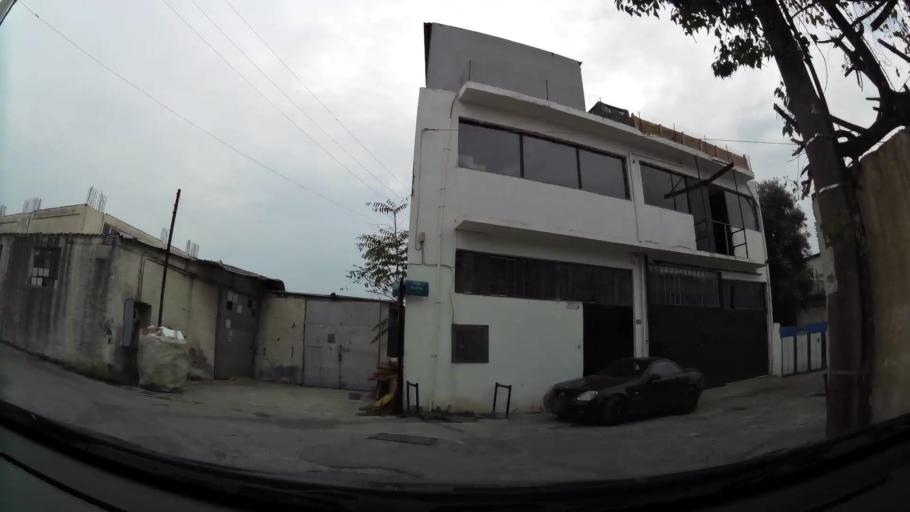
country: GR
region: Attica
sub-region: Nomarchia Athinas
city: Tavros
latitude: 37.9700
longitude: 23.6869
